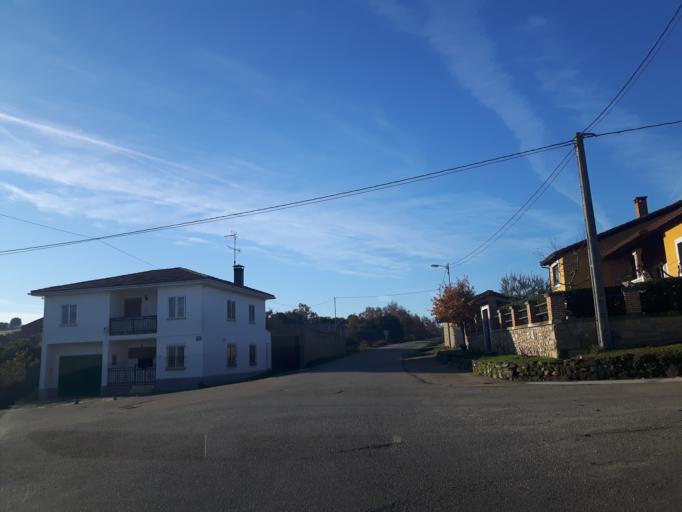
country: ES
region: Castille and Leon
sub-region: Provincia de Salamanca
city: Cerralbo
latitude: 40.9710
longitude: -6.5885
